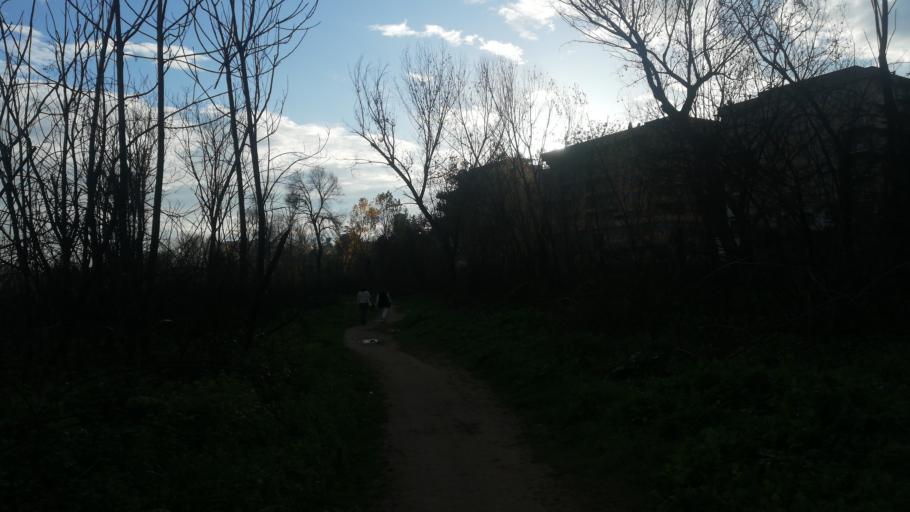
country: IT
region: Latium
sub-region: Citta metropolitana di Roma Capitale
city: Rome
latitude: 41.9309
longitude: 12.5299
